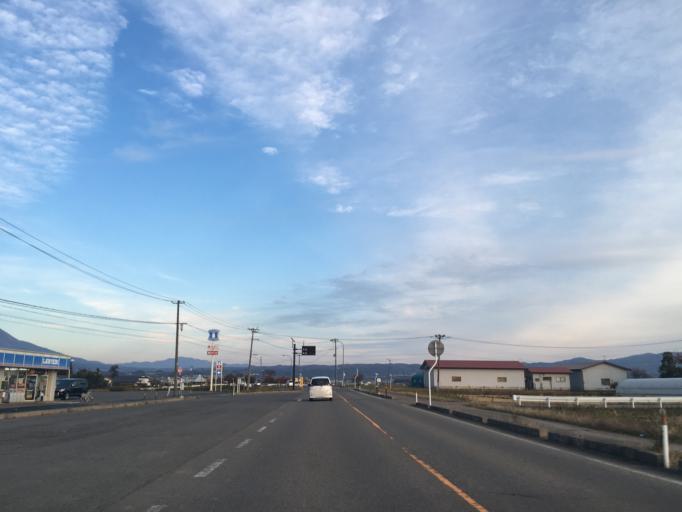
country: JP
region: Fukushima
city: Kitakata
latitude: 37.5531
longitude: 139.8817
